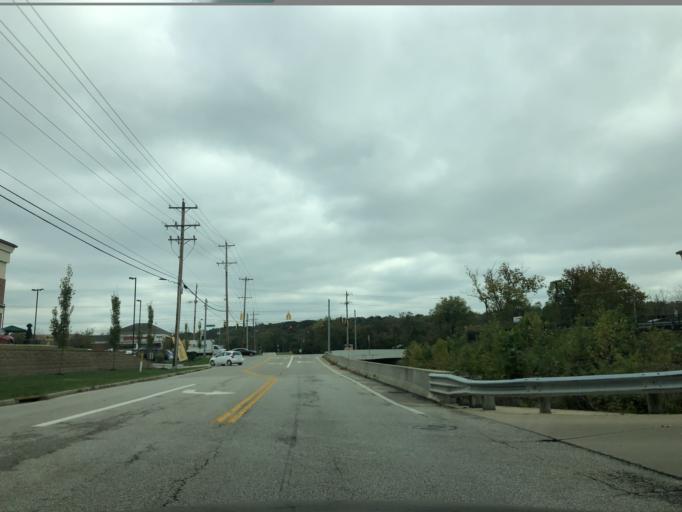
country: US
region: Ohio
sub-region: Hamilton County
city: The Village of Indian Hill
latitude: 39.2509
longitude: -84.2981
